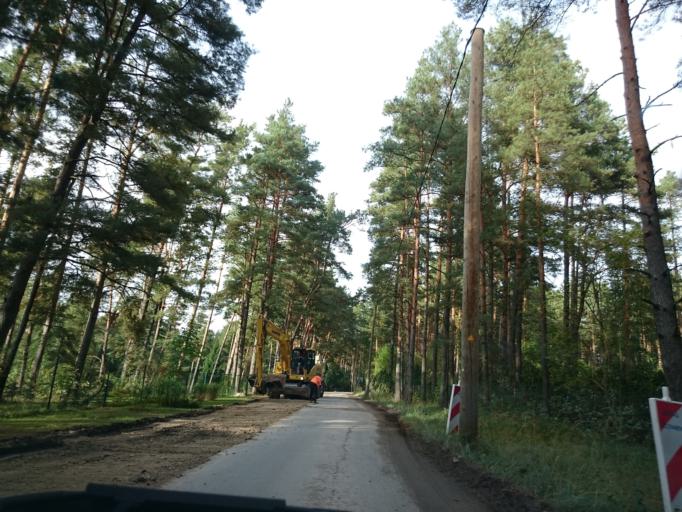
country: LV
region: Adazi
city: Adazi
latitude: 57.0441
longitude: 24.3375
